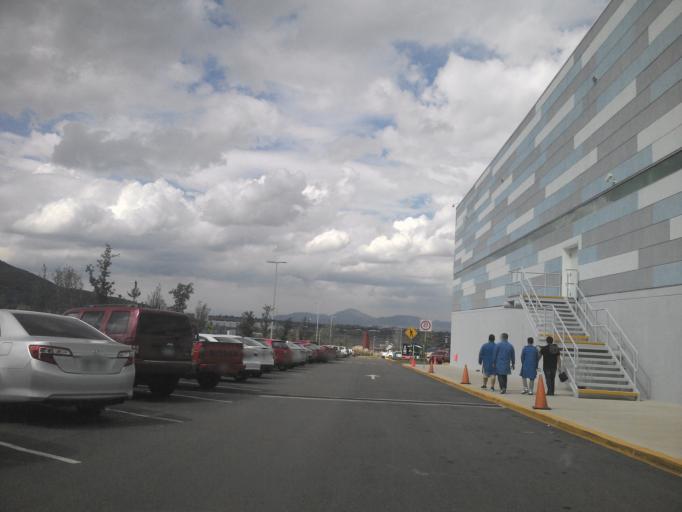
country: MX
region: Jalisco
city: Guadalajara
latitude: 20.6671
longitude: -103.4633
